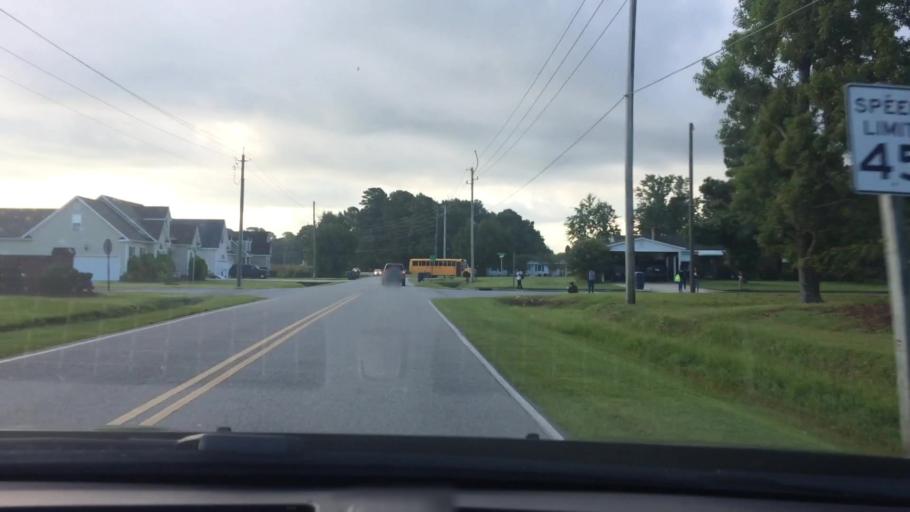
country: US
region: North Carolina
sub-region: Pitt County
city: Winterville
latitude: 35.5381
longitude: -77.3892
